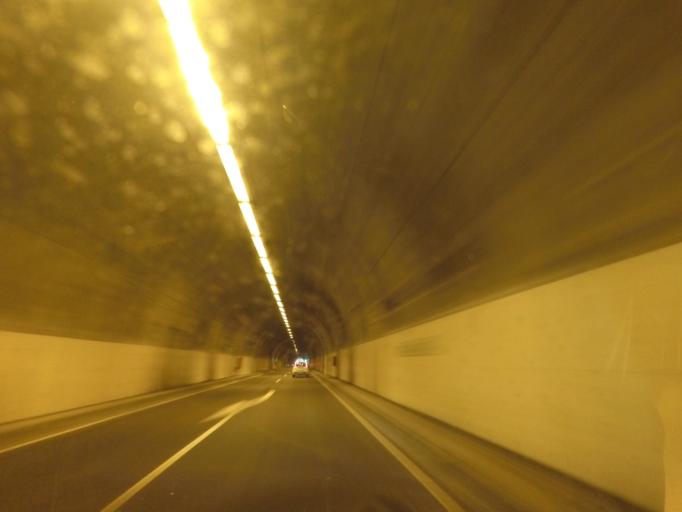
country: PT
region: Madeira
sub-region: Calheta
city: Estreito da Calheta
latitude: 32.7314
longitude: -17.1841
